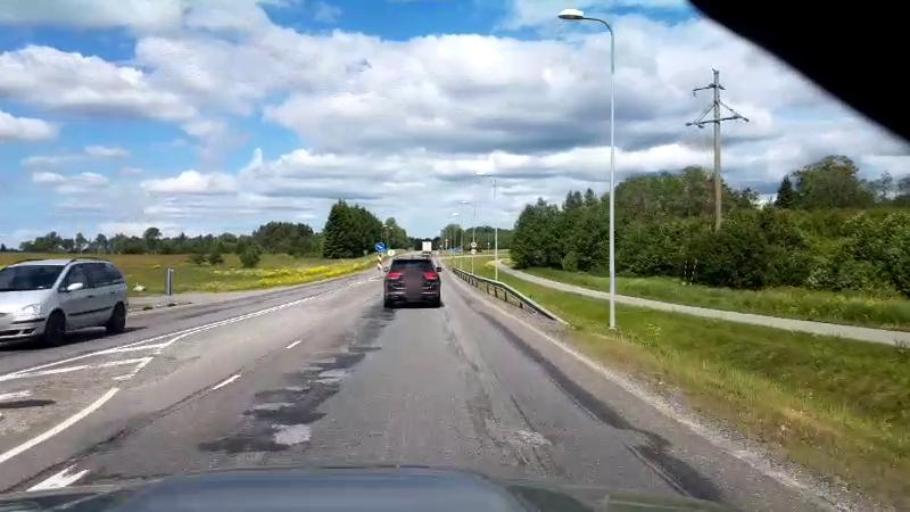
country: EE
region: Harju
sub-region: Keila linn
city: Keila
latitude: 59.1380
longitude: 24.5015
